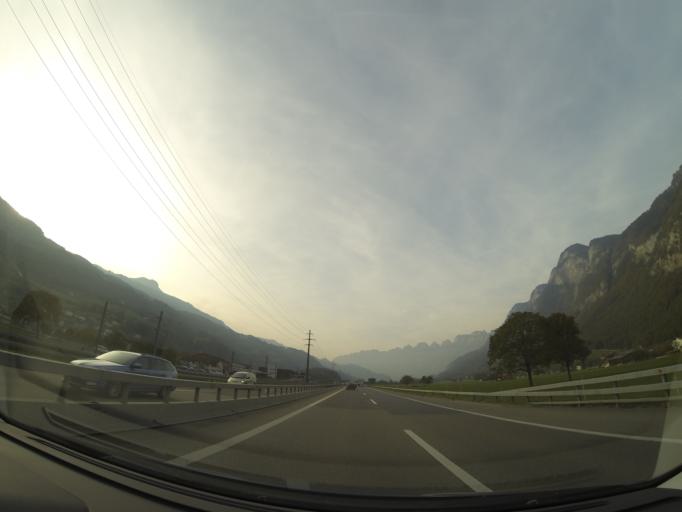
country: CH
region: Saint Gallen
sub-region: Wahlkreis Sarganserland
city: Sargans
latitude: 47.0566
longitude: 9.4062
